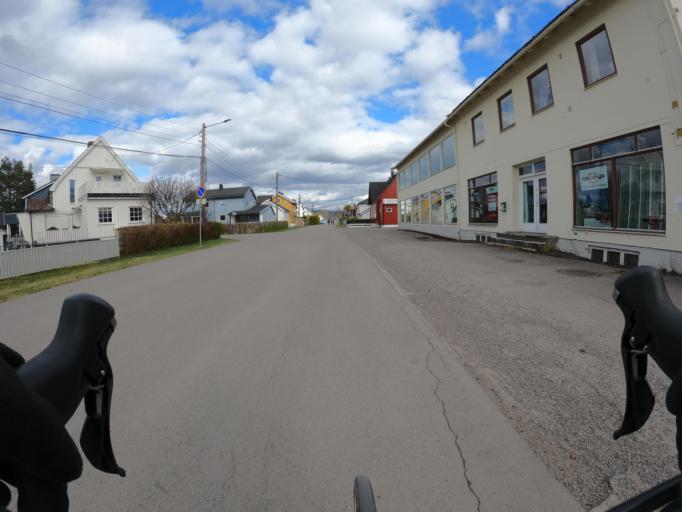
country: NO
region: Akershus
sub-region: Skedsmo
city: Lillestrom
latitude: 59.9543
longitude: 11.0566
